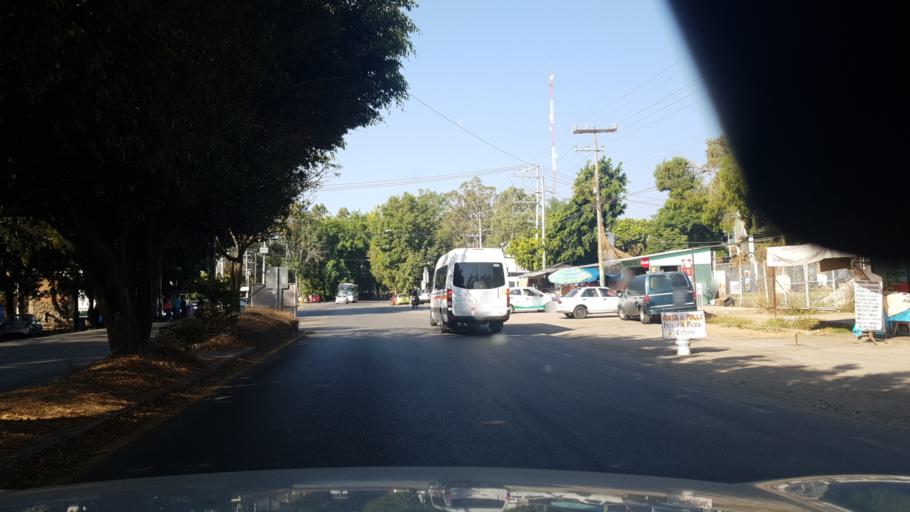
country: MX
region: Morelos
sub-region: Cuernavaca
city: Fraccionamiento Lomas de Ahuatlan
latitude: 18.9669
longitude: -99.2333
